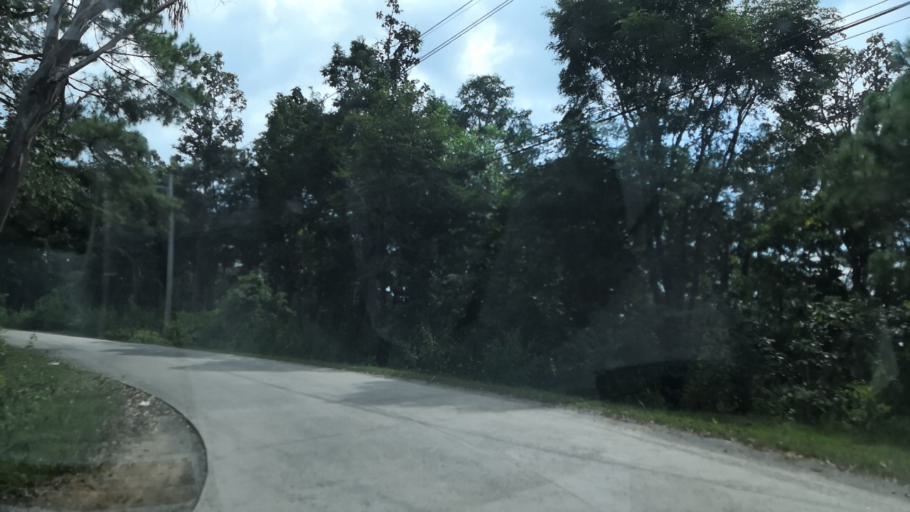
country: TH
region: Mae Hong Son
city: Khun Yuam
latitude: 18.8203
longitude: 97.9272
